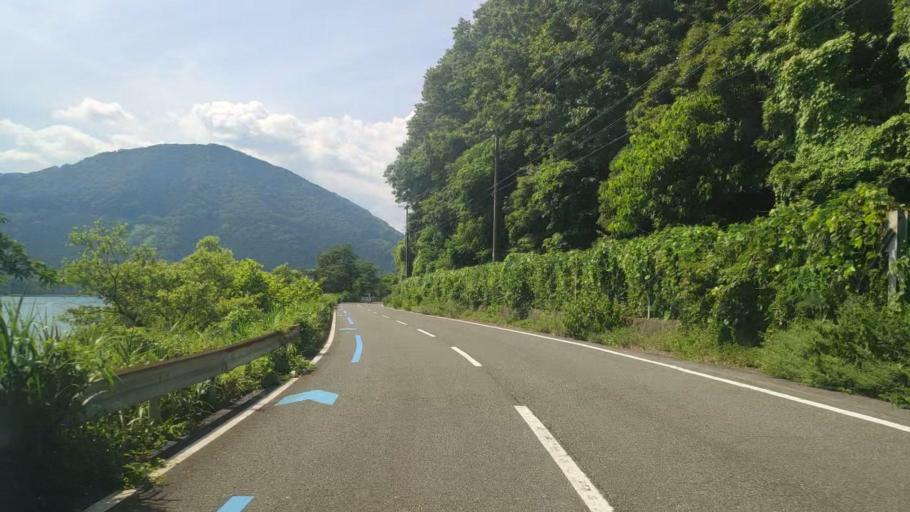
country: JP
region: Shiga Prefecture
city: Nagahama
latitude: 35.5013
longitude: 136.1719
